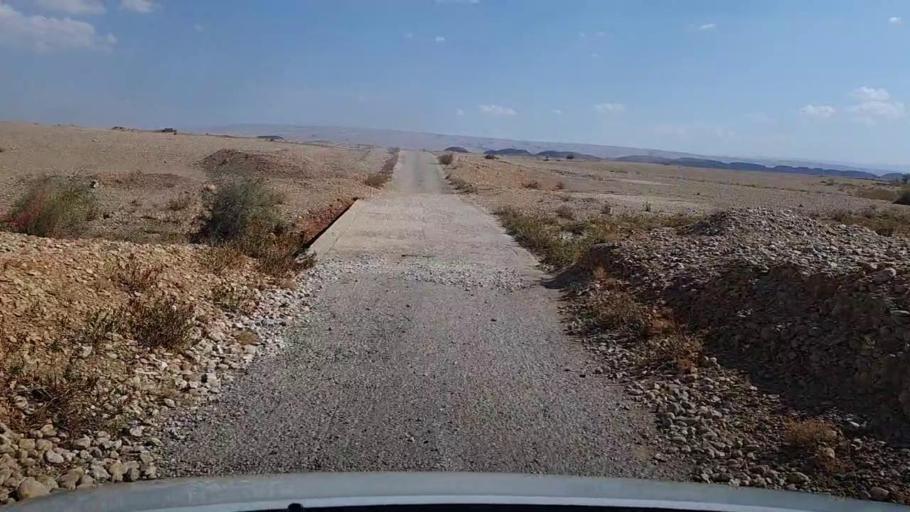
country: PK
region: Sindh
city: Bhan
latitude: 26.3679
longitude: 67.6406
